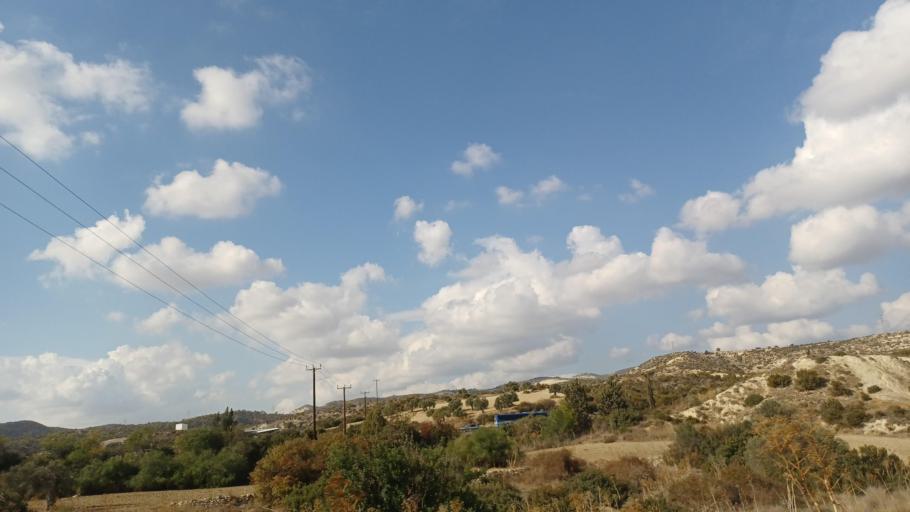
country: CY
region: Limassol
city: Pyrgos
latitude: 34.7359
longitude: 33.2857
